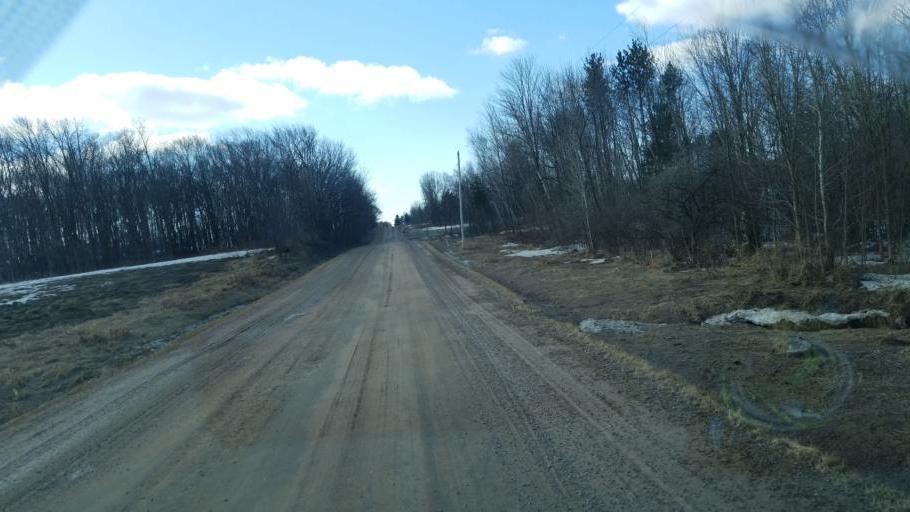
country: US
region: Wisconsin
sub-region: Clark County
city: Loyal
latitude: 44.6765
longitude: -90.4559
